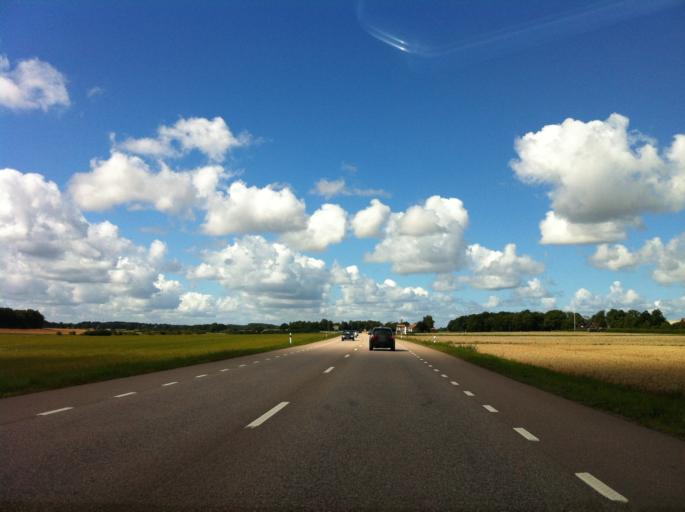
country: SE
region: Skane
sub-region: Bjuvs Kommun
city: Billesholm
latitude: 56.0709
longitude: 12.9636
